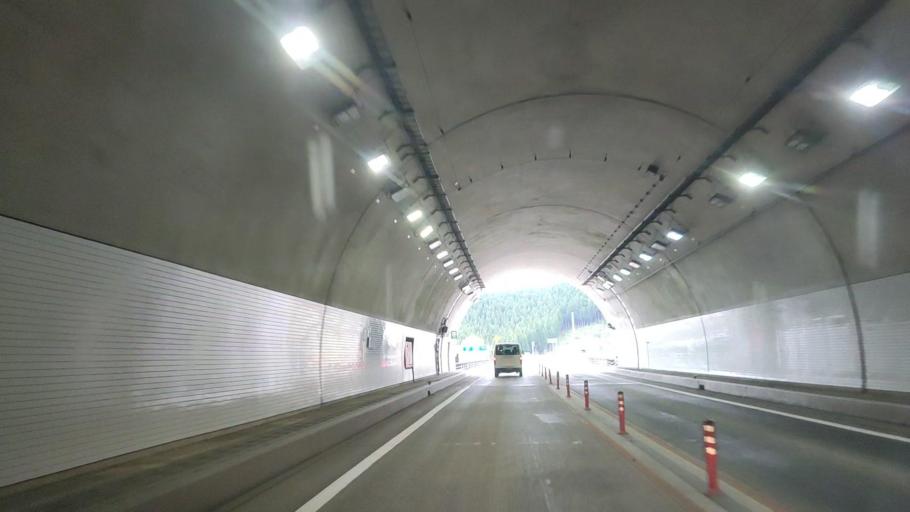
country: JP
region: Akita
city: Odate
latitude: 40.3287
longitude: 140.6069
